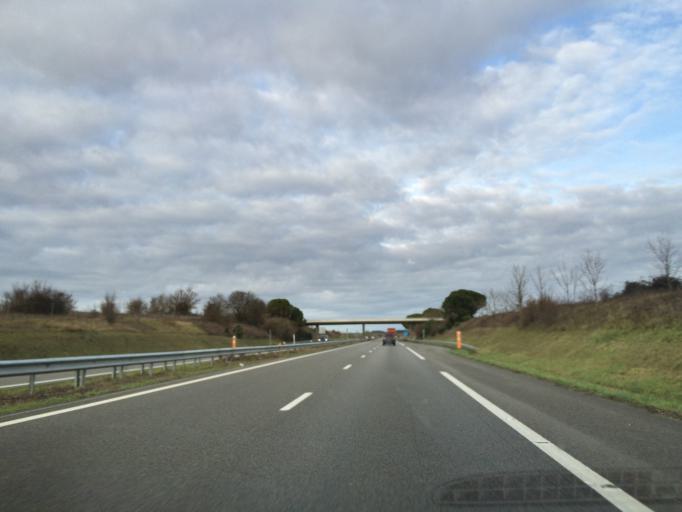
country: FR
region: Poitou-Charentes
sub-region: Departement de la Charente-Maritime
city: Saint-Jean-d'Angely
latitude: 45.9862
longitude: -0.5449
